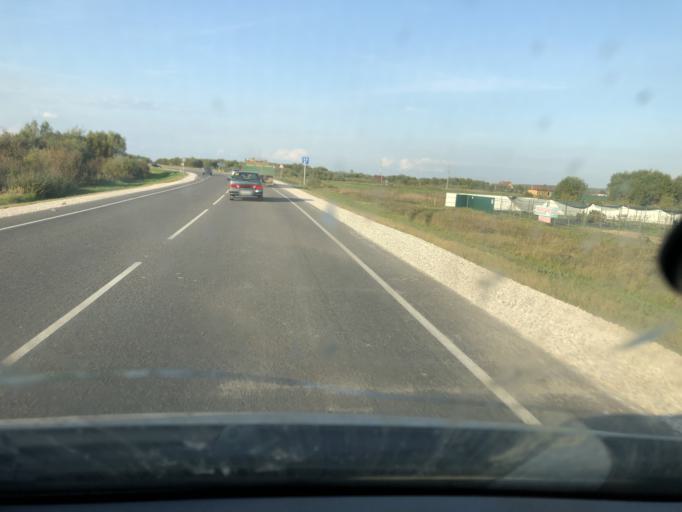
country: RU
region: Kaluga
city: Peremyshl'
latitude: 54.2622
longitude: 36.1316
